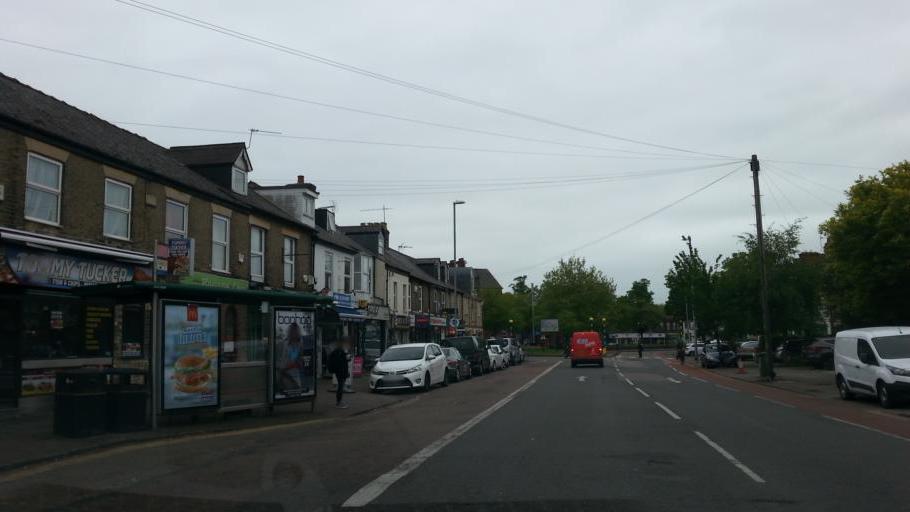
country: GB
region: England
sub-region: Cambridgeshire
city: Cambridge
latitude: 52.2155
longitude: 0.1257
